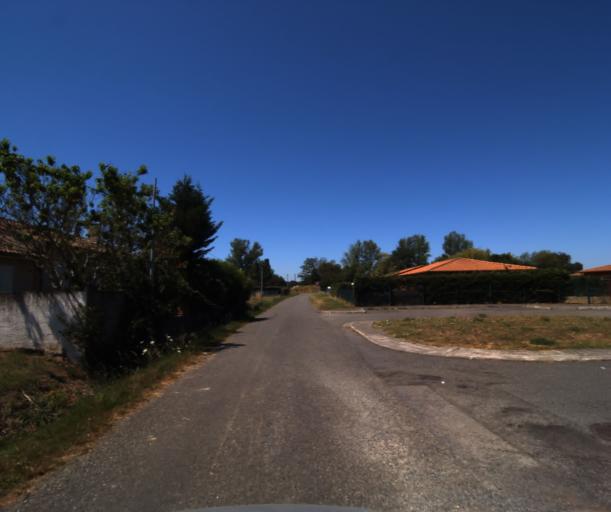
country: FR
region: Midi-Pyrenees
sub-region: Departement de la Haute-Garonne
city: Seysses
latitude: 43.4701
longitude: 1.3105
